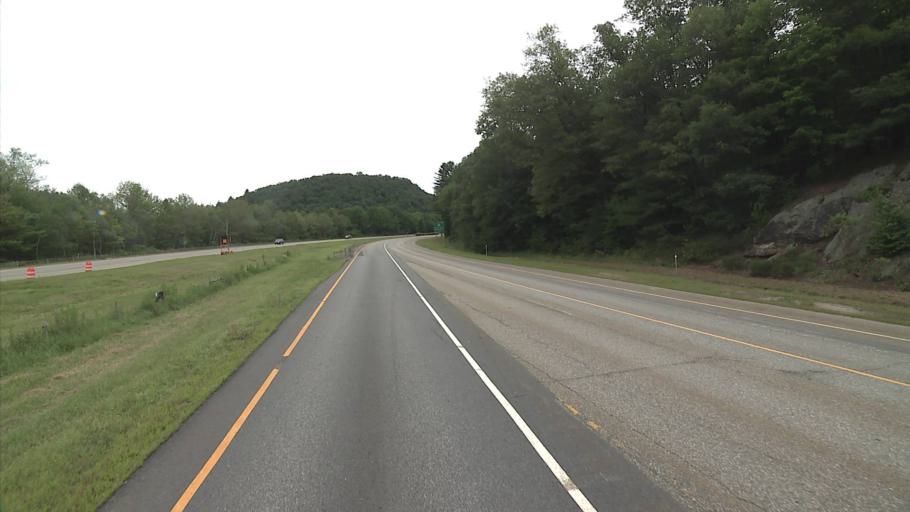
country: US
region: Connecticut
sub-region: Litchfield County
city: Northwest Harwinton
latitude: 41.7430
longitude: -73.1129
